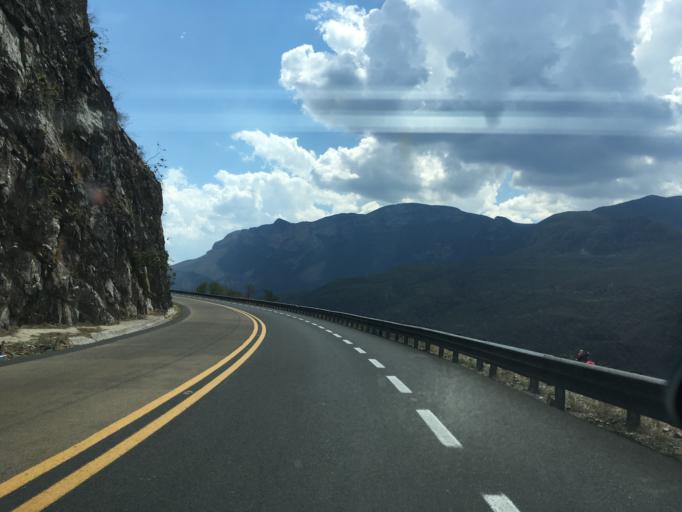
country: MX
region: Puebla
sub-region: San Jose Miahuatlan
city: San Pedro Tetitlan
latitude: 18.1540
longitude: -97.3035
